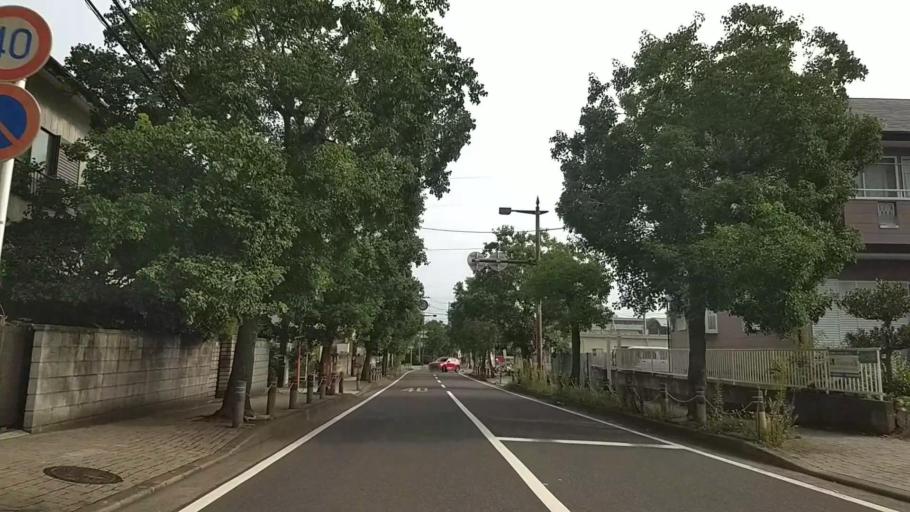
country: JP
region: Kanagawa
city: Oiso
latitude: 35.3302
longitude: 139.3098
